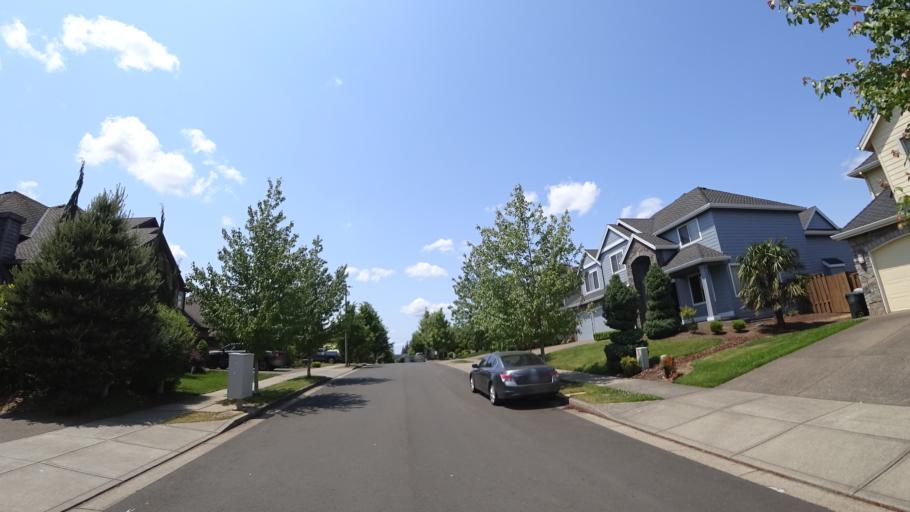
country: US
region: Oregon
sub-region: Clackamas County
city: Happy Valley
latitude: 45.4447
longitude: -122.5466
